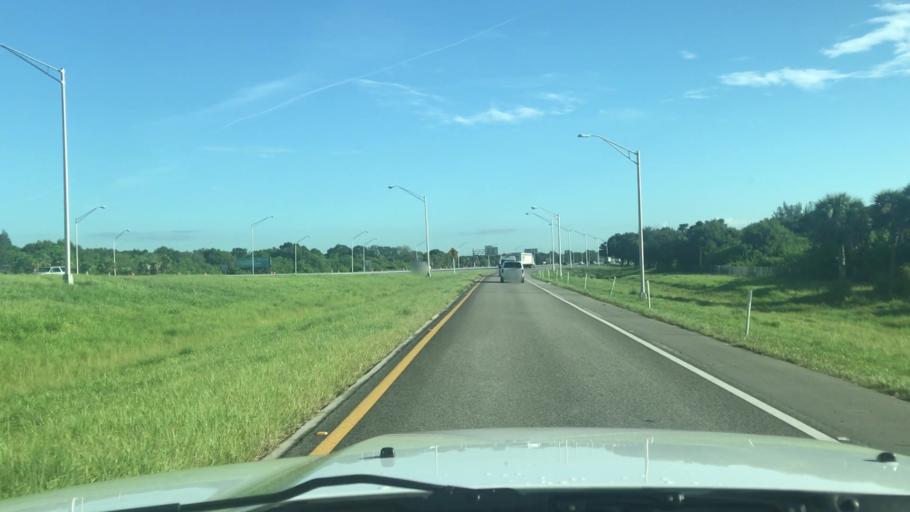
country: US
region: Florida
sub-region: Saint Lucie County
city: Fort Pierce South
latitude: 27.4187
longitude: -80.3878
